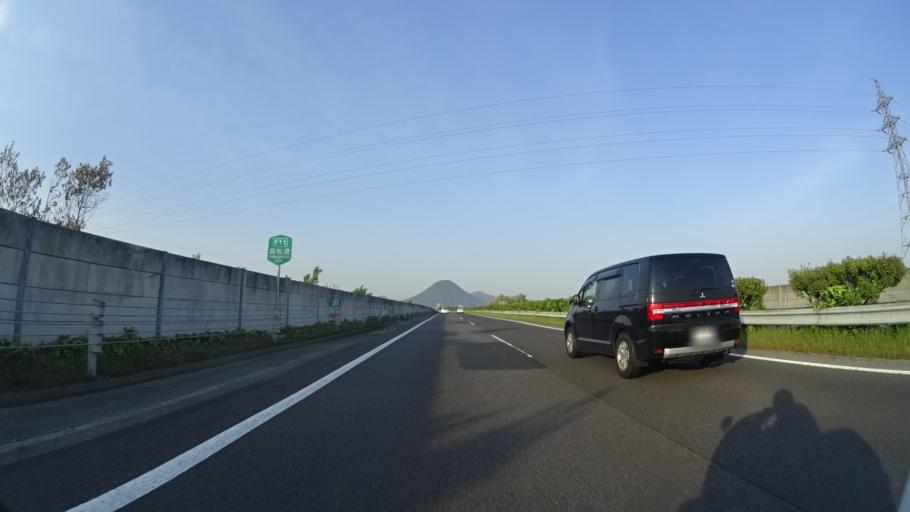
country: JP
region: Kagawa
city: Marugame
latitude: 34.2453
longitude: 133.7922
